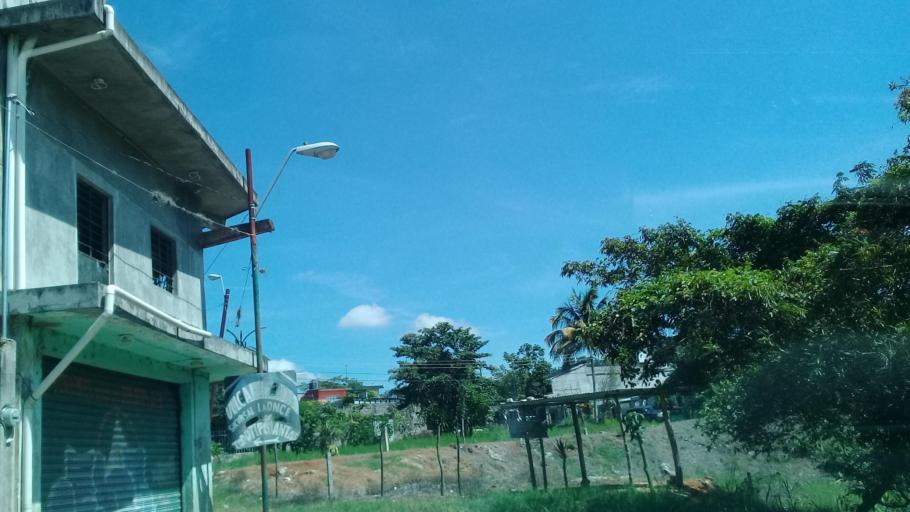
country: MX
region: Veracruz
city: Amatlan de los Reyes
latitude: 18.8406
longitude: -96.9178
